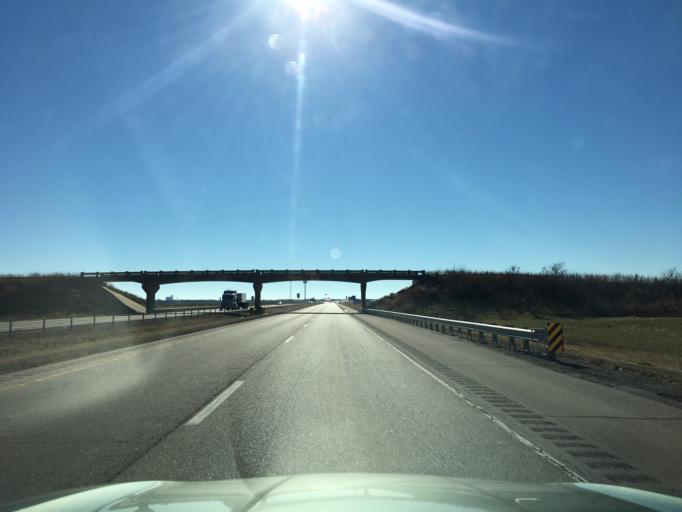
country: US
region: Oklahoma
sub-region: Kay County
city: Blackwell
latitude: 36.9570
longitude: -97.3458
